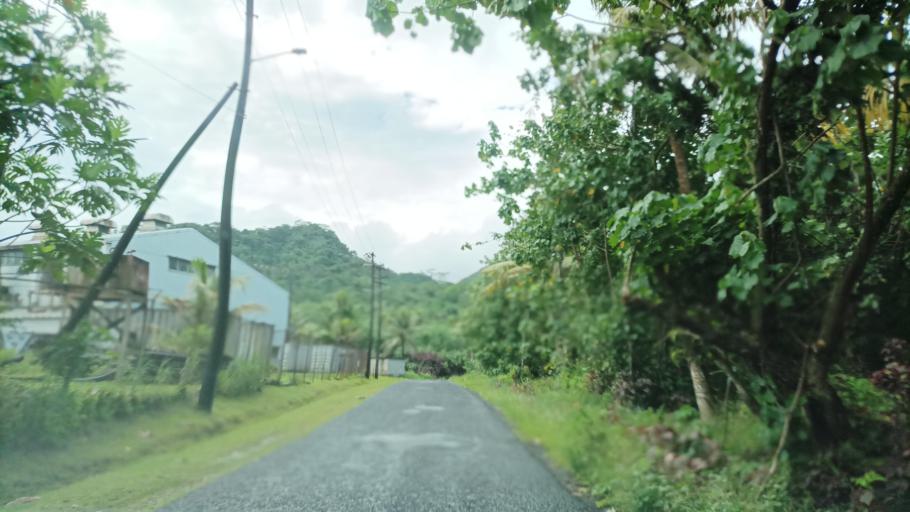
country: FM
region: Pohnpei
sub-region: Sokehs Municipality
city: Palikir - National Government Center
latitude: 6.9351
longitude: 158.1909
